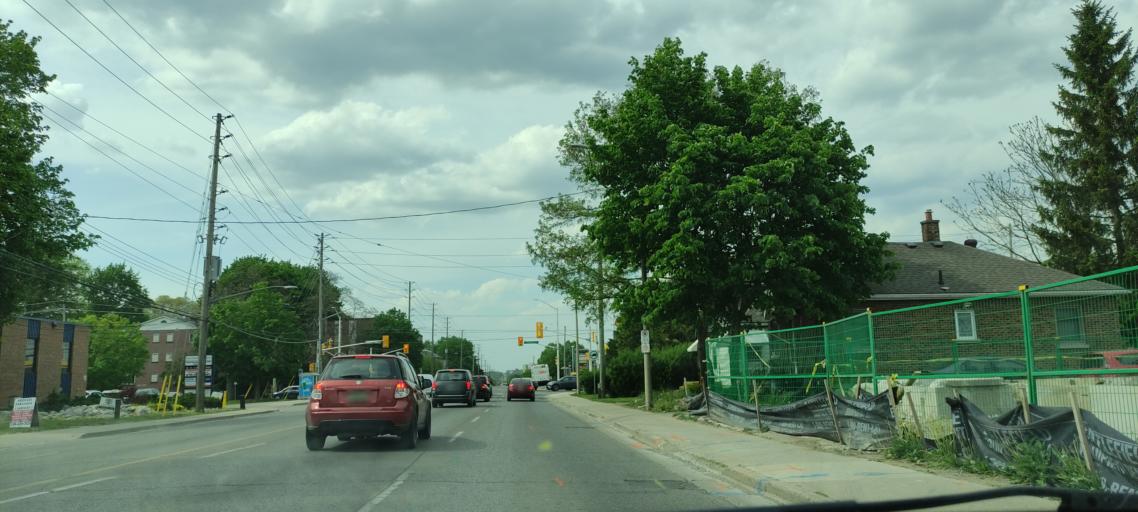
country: CA
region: Ontario
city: London
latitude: 43.0053
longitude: -81.2396
